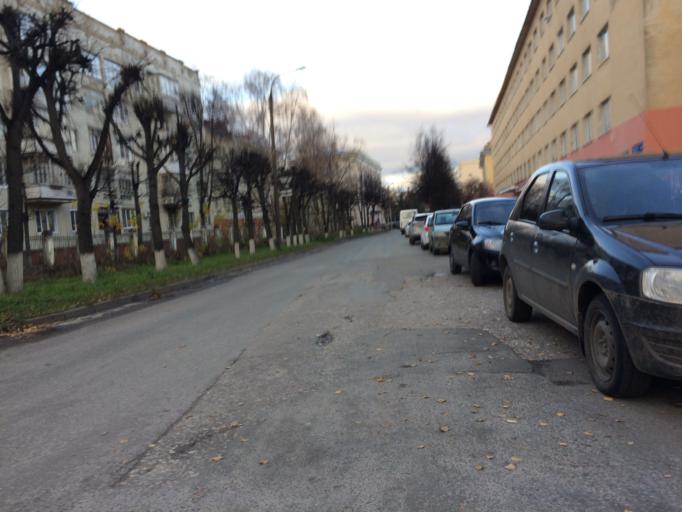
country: RU
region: Mariy-El
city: Yoshkar-Ola
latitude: 56.6287
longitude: 47.8906
